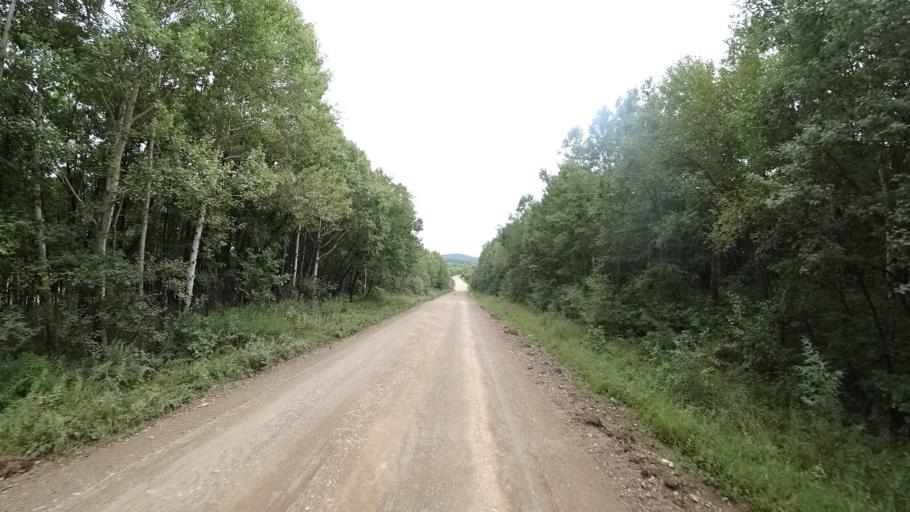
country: RU
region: Primorskiy
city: Lyalichi
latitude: 44.0847
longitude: 132.4431
